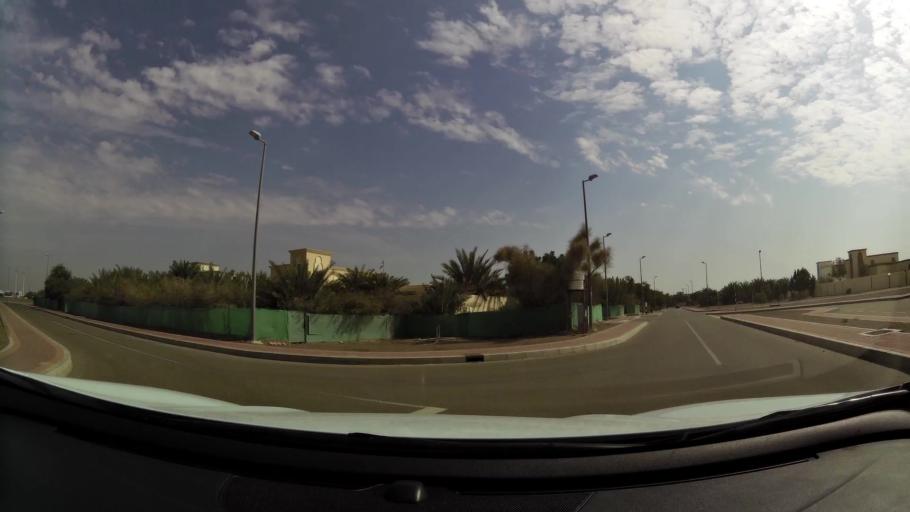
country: AE
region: Abu Dhabi
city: Al Ain
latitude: 24.0981
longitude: 55.8936
